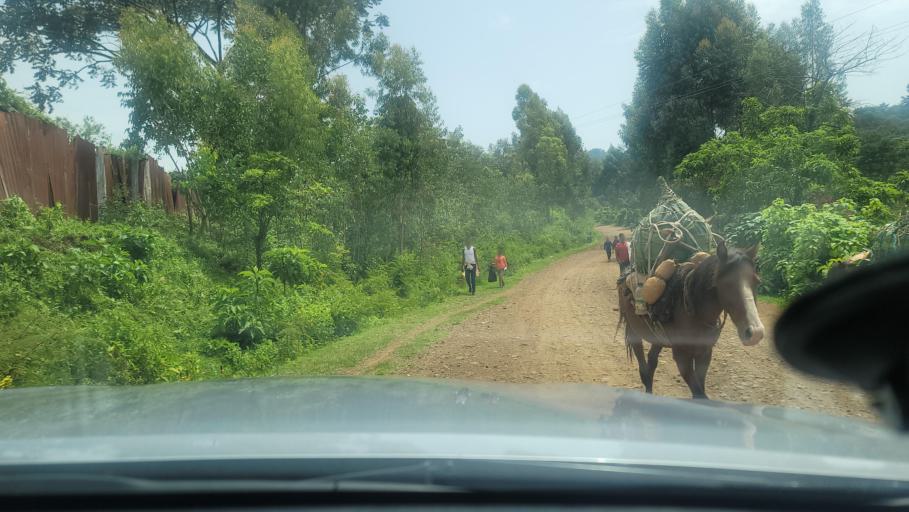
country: ET
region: Oromiya
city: Agaro
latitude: 7.7988
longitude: 36.4170
